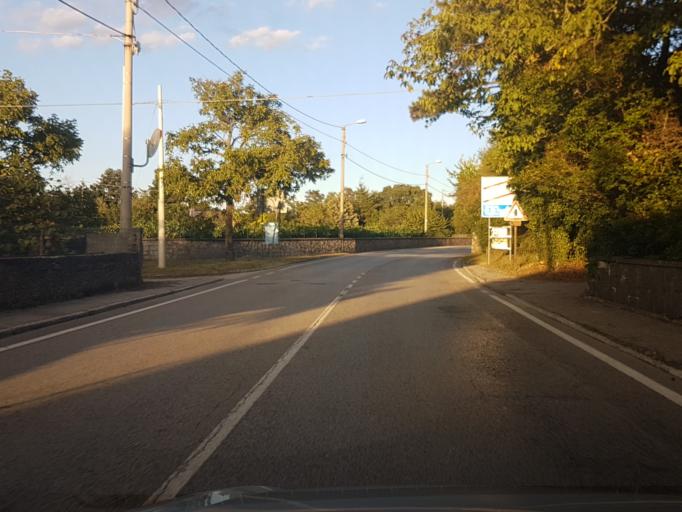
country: IT
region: Friuli Venezia Giulia
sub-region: Provincia di Trieste
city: Prosecco-Contovello
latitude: 45.7074
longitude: 13.7379
